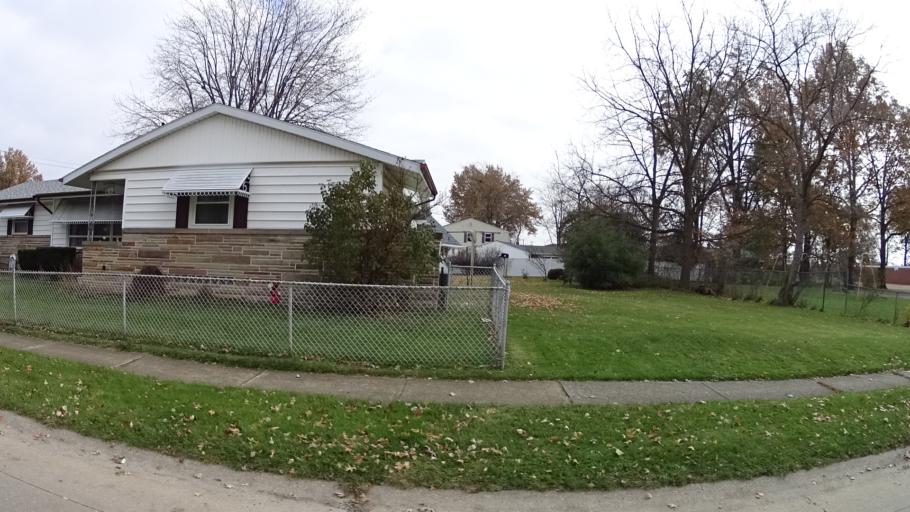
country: US
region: Ohio
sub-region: Lorain County
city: Elyria
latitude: 41.3646
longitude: -82.0804
